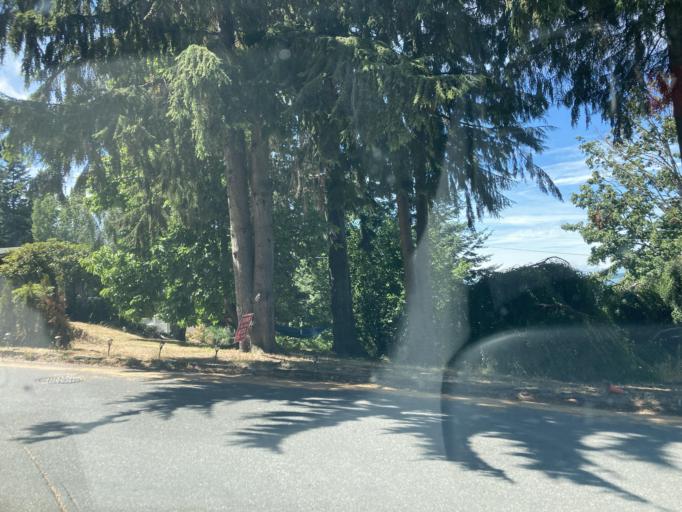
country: US
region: Washington
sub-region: Whatcom County
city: Bellingham
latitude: 48.7318
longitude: -122.4956
